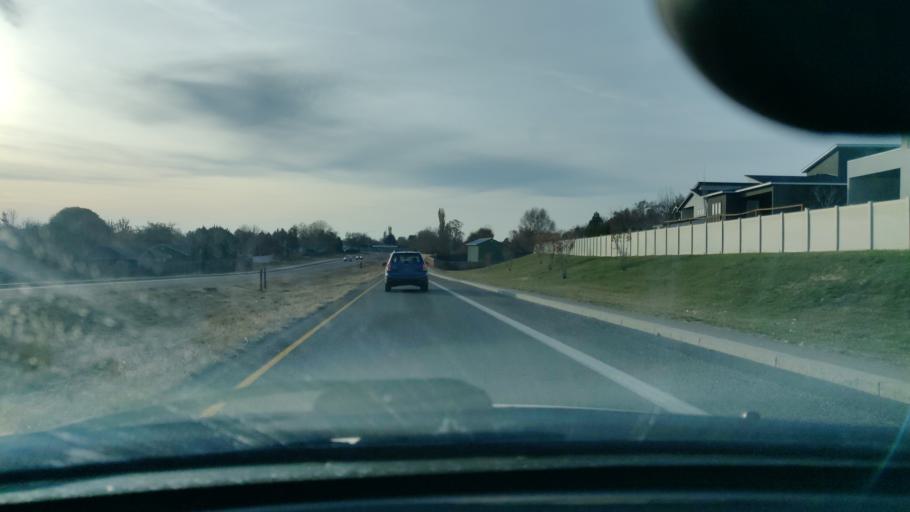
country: US
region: Idaho
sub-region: Ada County
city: Eagle
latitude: 43.6849
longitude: -116.2823
